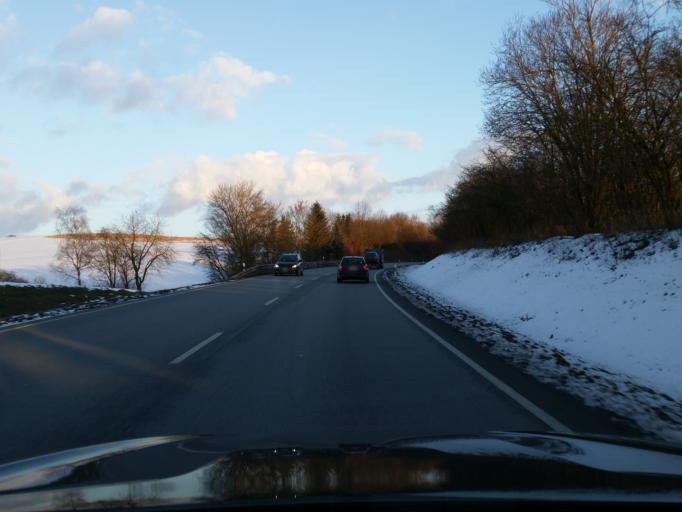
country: DE
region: Bavaria
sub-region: Lower Bavaria
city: Weihmichl
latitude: 48.5772
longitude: 12.0795
